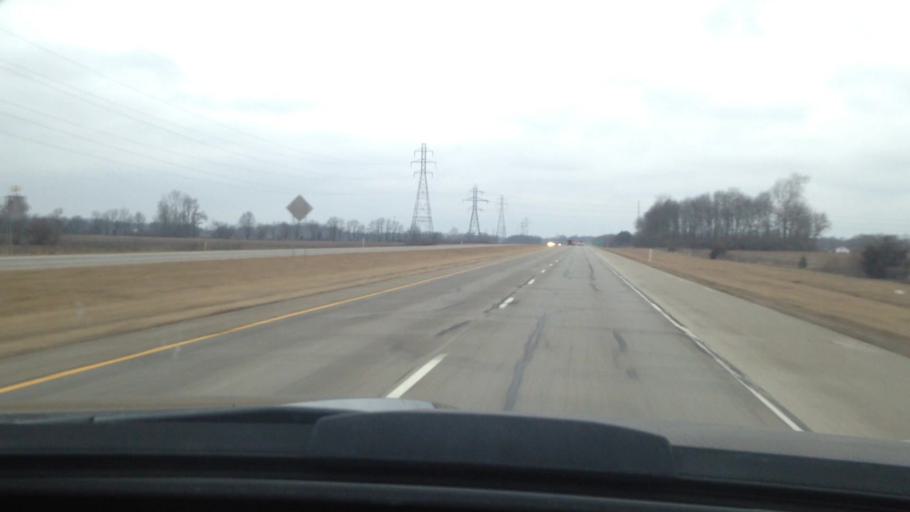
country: US
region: Indiana
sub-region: Delaware County
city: Muncie
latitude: 40.1424
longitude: -85.4078
